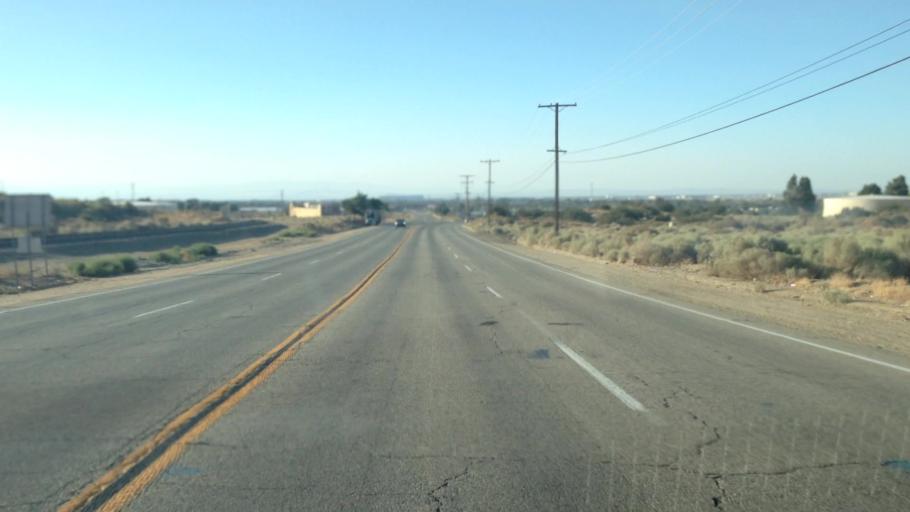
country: US
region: California
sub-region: Los Angeles County
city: Palmdale
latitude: 34.5539
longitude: -118.1140
